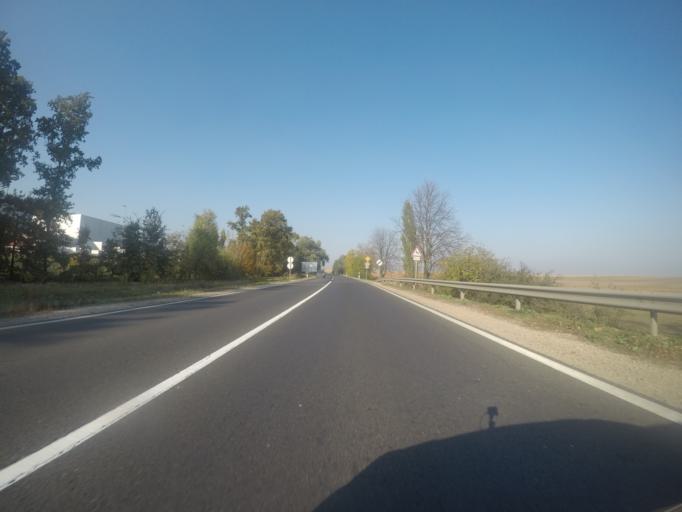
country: HU
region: Fejer
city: Racalmas
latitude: 47.0011
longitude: 18.9306
